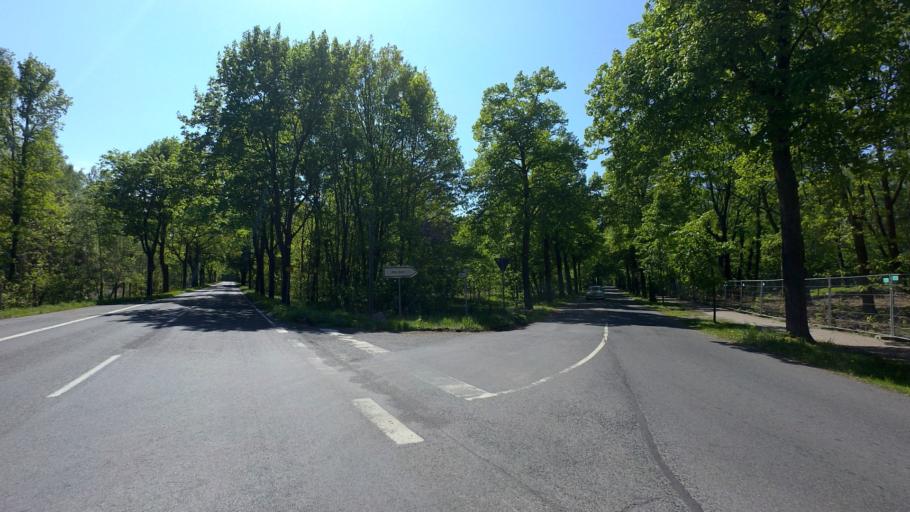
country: DE
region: Brandenburg
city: Bestensee
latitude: 52.2322
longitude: 13.6684
